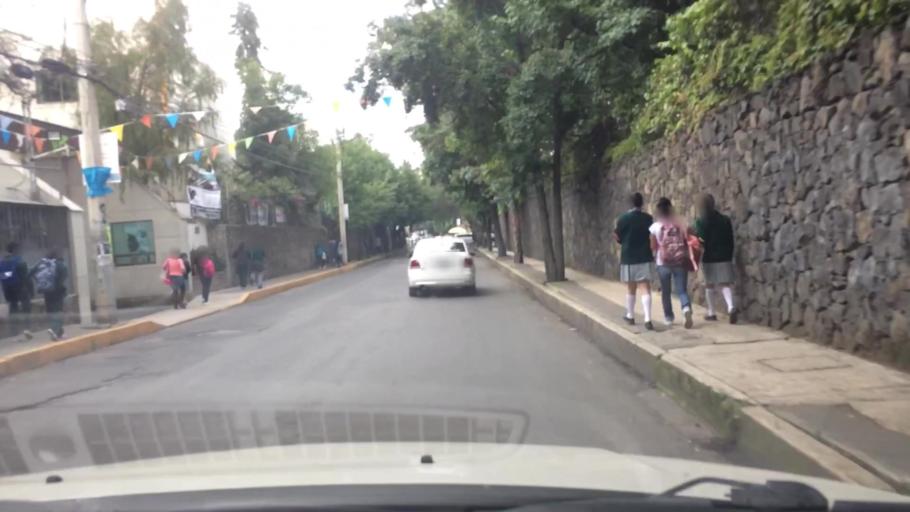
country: MX
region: Mexico City
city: Xochimilco
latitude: 19.2699
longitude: -99.1398
